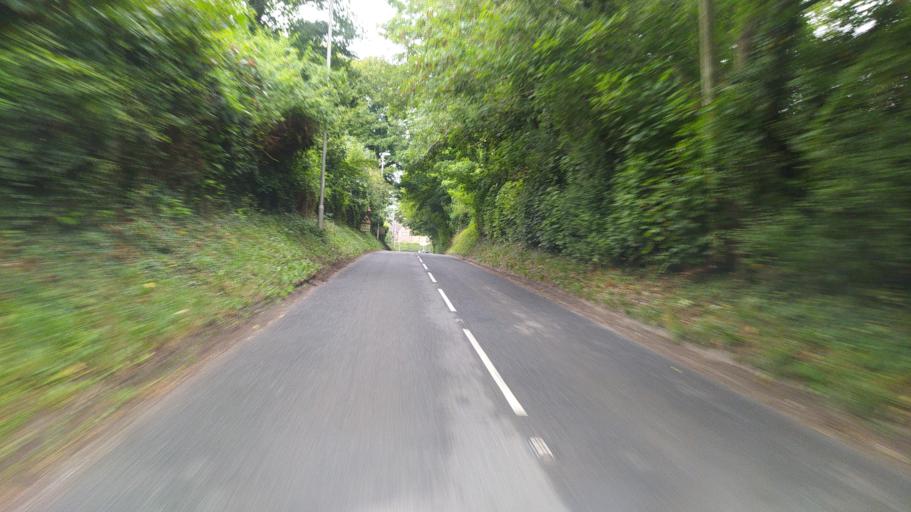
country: GB
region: England
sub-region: Wiltshire
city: Bower Chalke
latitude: 50.9517
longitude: -2.0004
